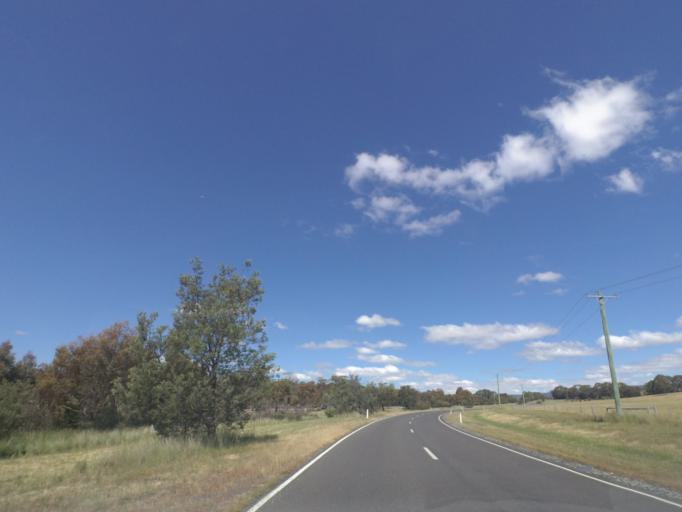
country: AU
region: Victoria
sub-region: Hume
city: Sunbury
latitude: -37.2974
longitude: 144.5044
